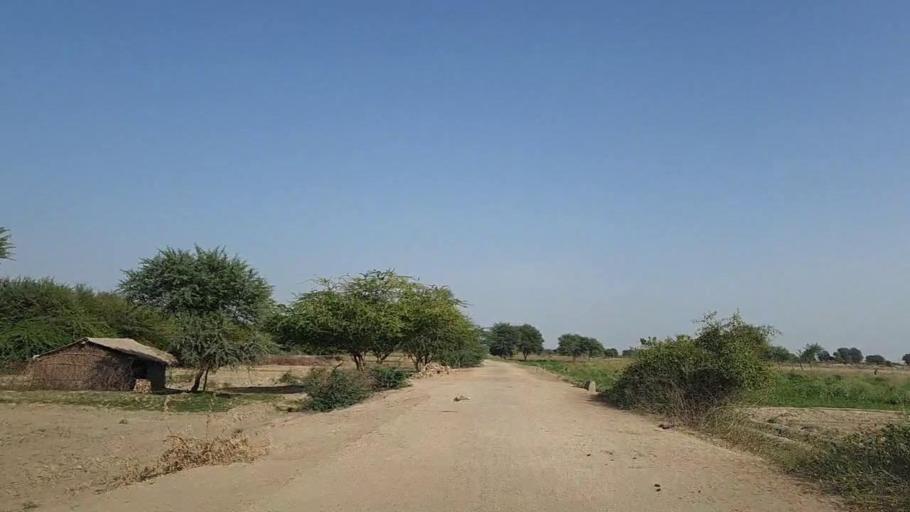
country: PK
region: Sindh
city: Dhoro Naro
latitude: 25.4167
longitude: 69.5246
